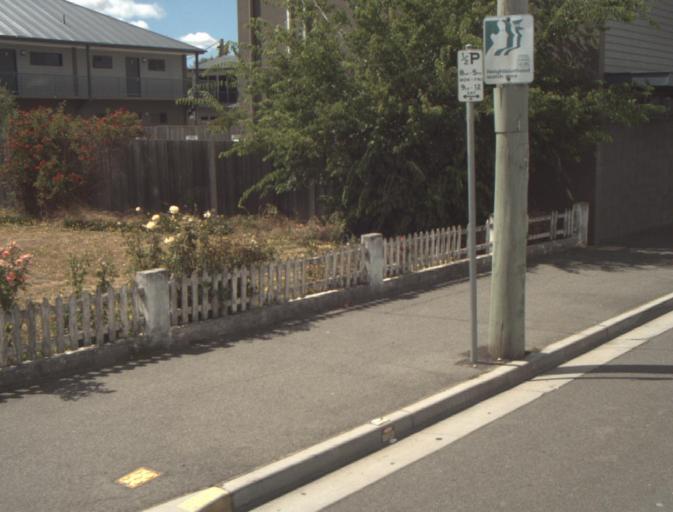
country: AU
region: Tasmania
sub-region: Launceston
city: Launceston
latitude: -41.4206
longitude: 147.1354
